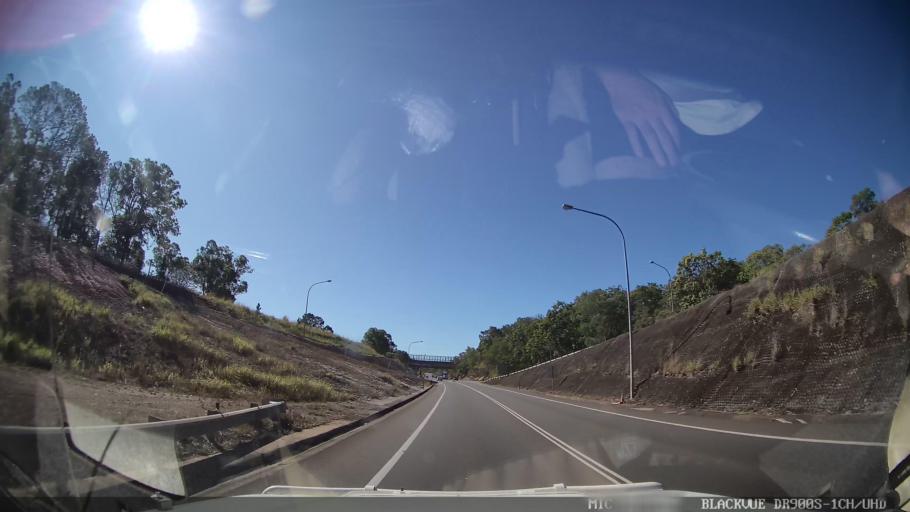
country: AU
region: Queensland
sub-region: Fraser Coast
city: Maryborough
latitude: -25.5191
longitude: 152.6688
